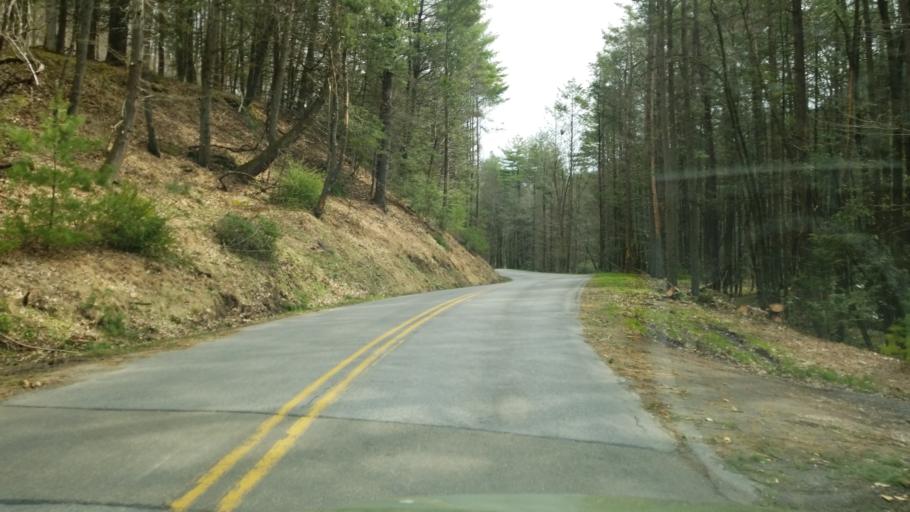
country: US
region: Pennsylvania
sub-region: Cameron County
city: Emporium
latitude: 41.2978
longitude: -78.1081
